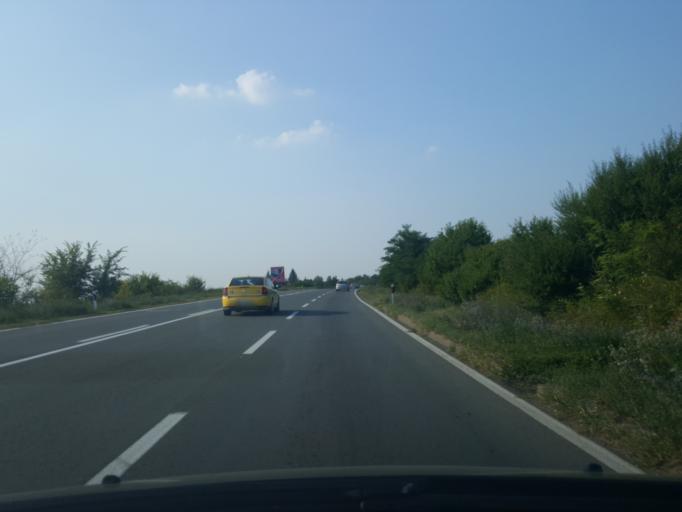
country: RS
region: Central Serbia
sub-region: Belgrade
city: Sopot
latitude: 44.5158
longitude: 20.6527
